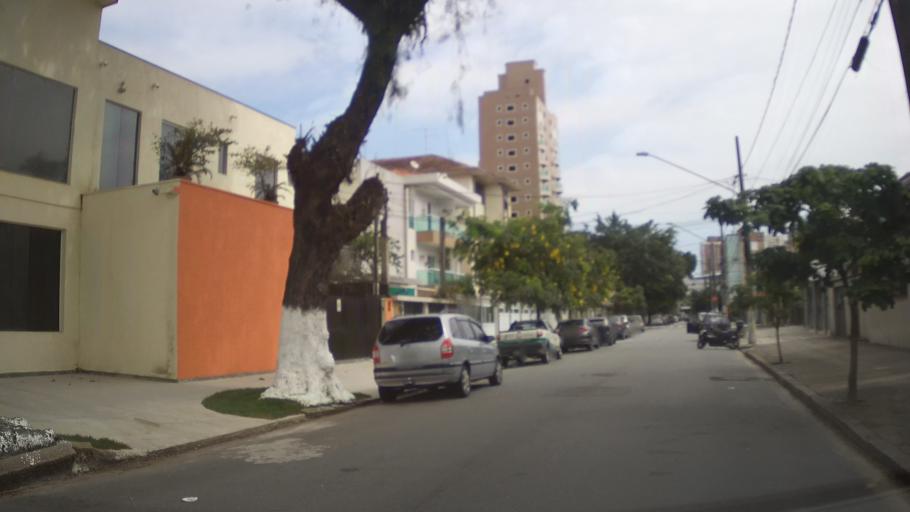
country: BR
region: Sao Paulo
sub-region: Santos
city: Santos
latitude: -23.9607
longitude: -46.3178
